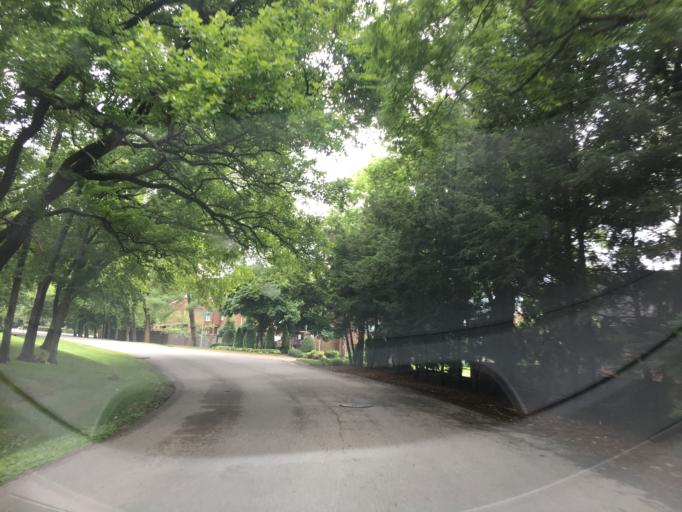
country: US
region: Tennessee
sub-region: Davidson County
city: Belle Meade
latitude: 36.0930
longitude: -86.8331
